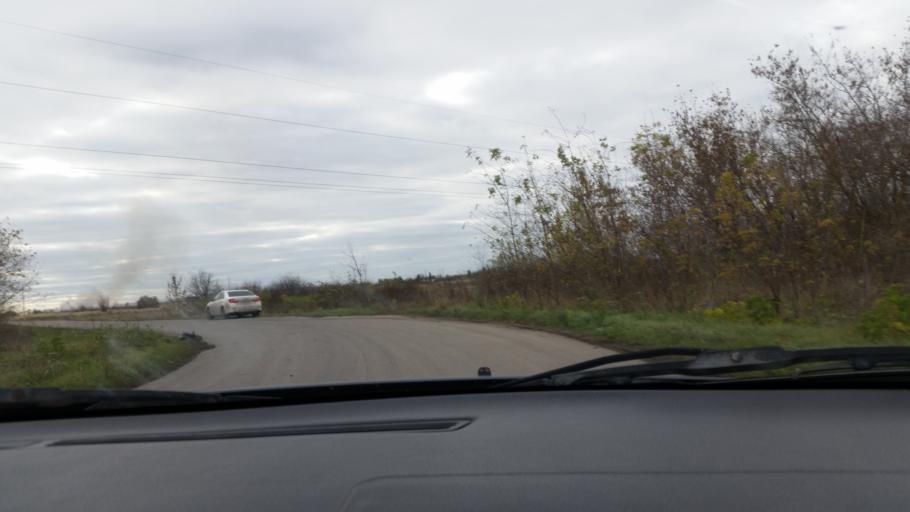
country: RU
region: Lipetsk
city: Gryazi
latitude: 52.4672
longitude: 39.9364
